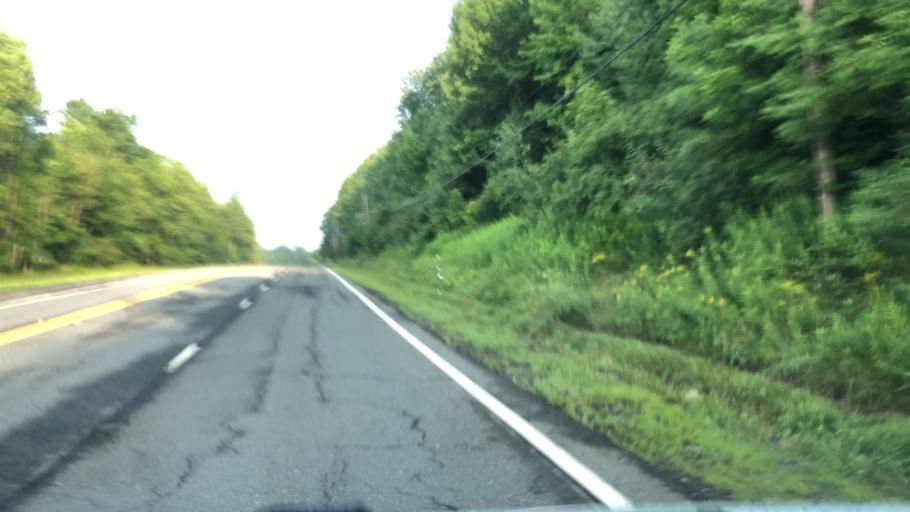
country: US
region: Massachusetts
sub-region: Berkshire County
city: Hinsdale
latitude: 42.4971
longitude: -73.0118
